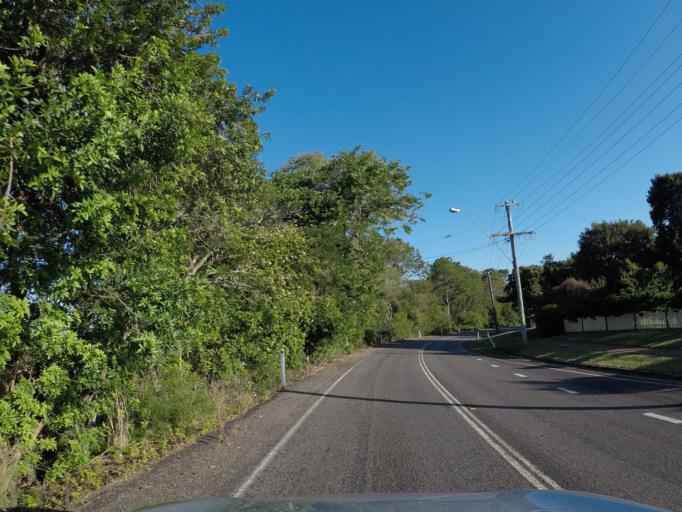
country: AU
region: Queensland
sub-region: Sunshine Coast
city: Nambour
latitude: -26.6284
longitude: 152.8676
